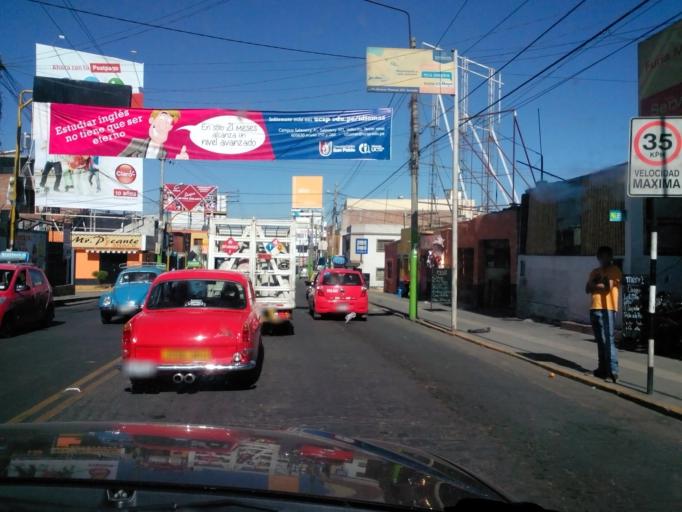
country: PE
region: Arequipa
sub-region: Provincia de Arequipa
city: Arequipa
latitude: -16.3863
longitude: -71.5541
